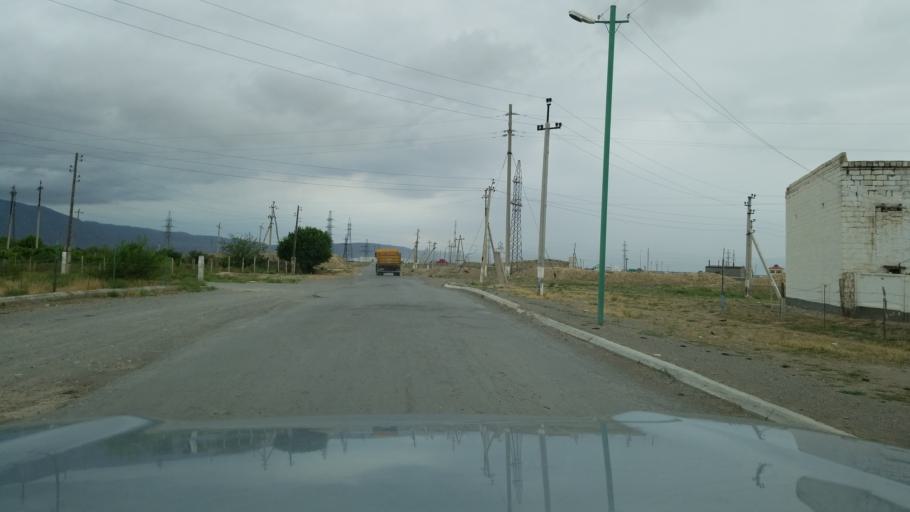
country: TM
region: Balkan
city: Serdar
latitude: 38.9749
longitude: 56.2532
